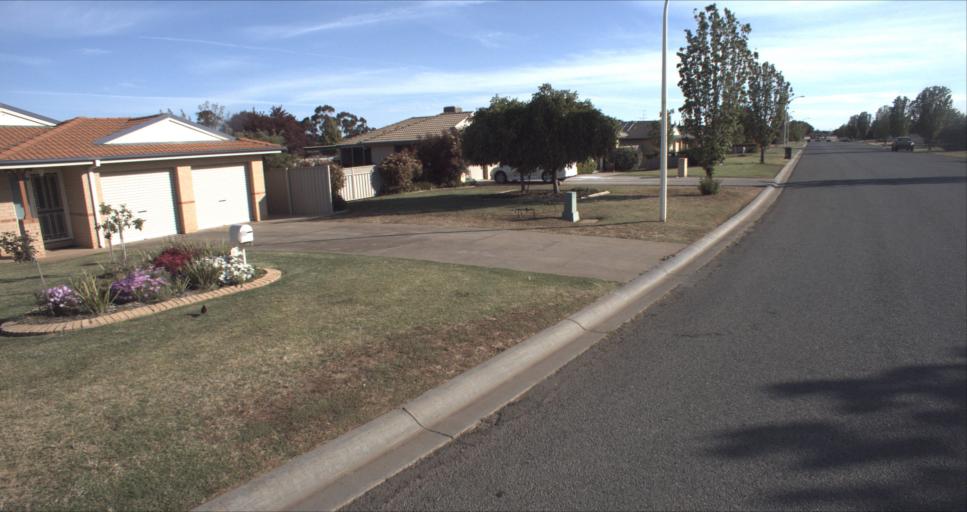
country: AU
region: New South Wales
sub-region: Leeton
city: Leeton
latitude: -34.5390
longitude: 146.4031
